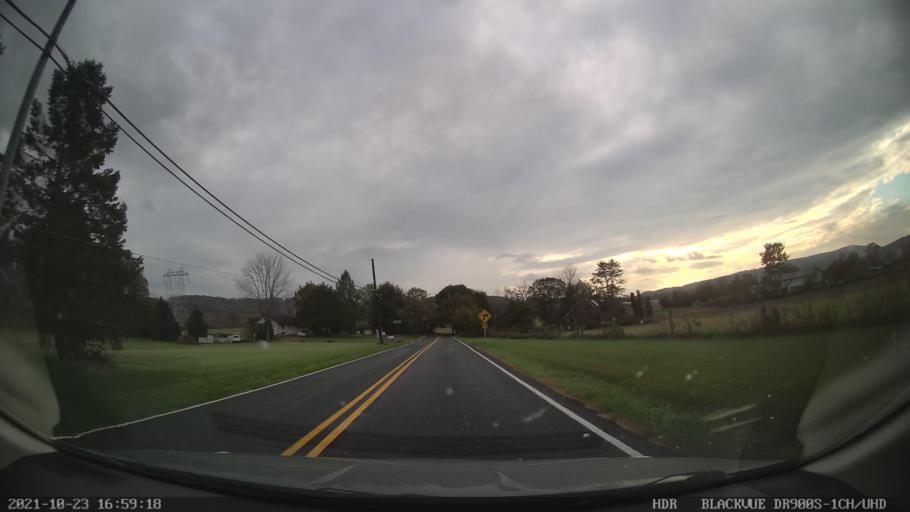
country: US
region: Pennsylvania
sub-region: Montgomery County
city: East Greenville
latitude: 40.4299
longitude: -75.5434
